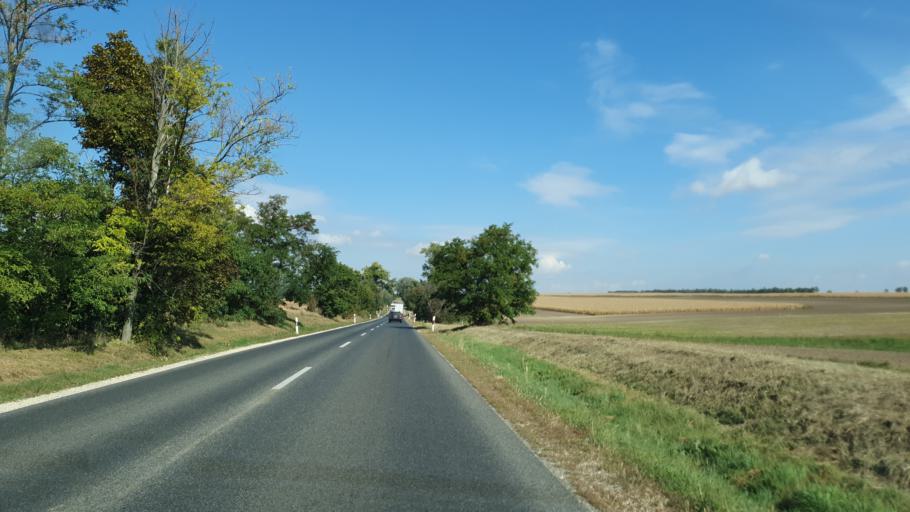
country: HU
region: Fejer
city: Szekesfehervar
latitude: 47.2482
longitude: 18.4185
